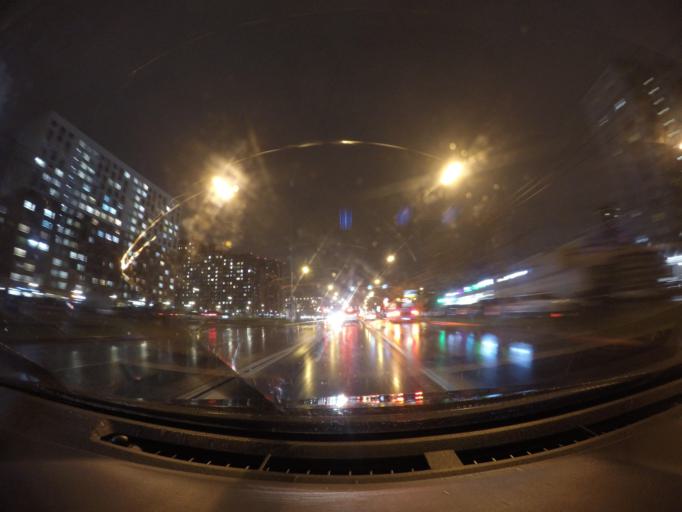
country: RU
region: Moscow
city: Orekhovo-Borisovo
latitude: 55.6038
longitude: 37.7271
